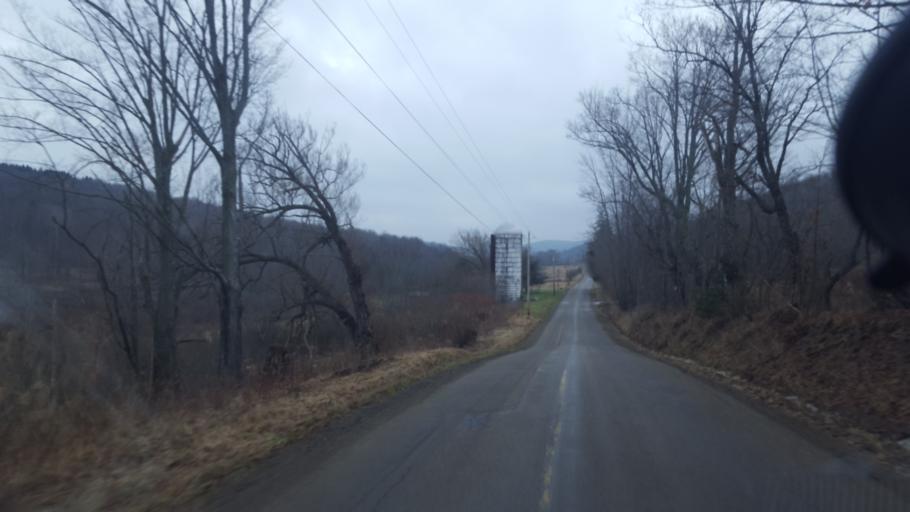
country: US
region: Pennsylvania
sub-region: Tioga County
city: Westfield
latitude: 41.9689
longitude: -77.7196
